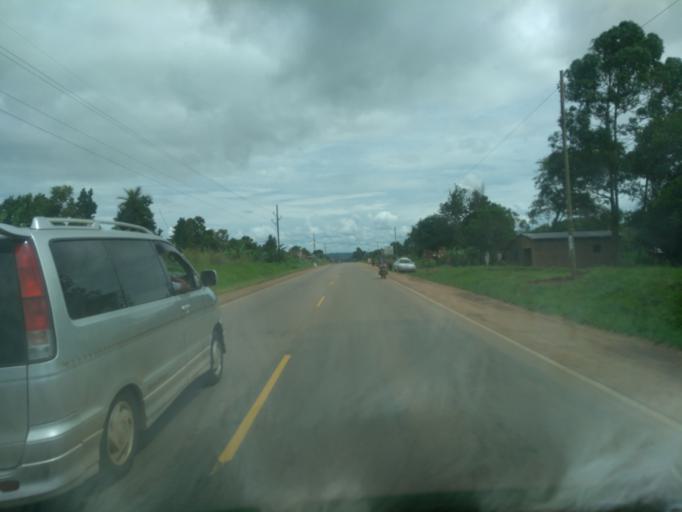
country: UG
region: Central Region
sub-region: Butambala District
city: Gombe
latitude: -0.0042
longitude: 32.0370
